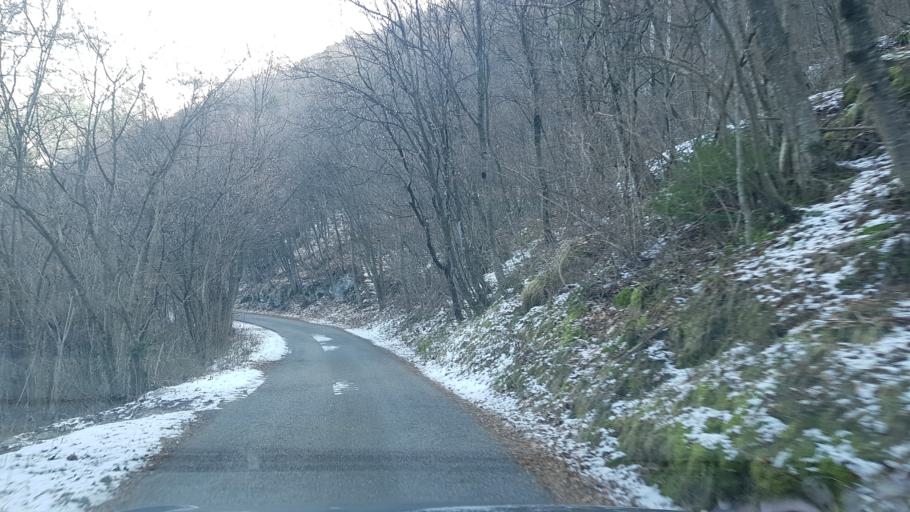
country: IT
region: Friuli Venezia Giulia
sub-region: Provincia di Udine
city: Montenars
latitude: 46.2798
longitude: 13.1548
